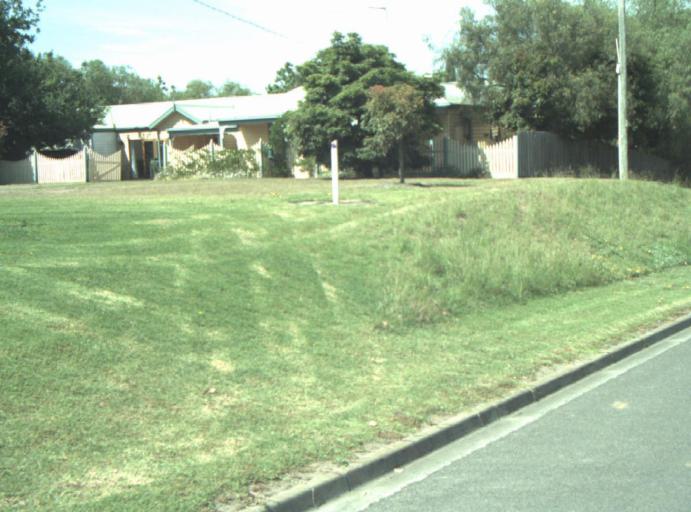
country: AU
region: Victoria
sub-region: Greater Geelong
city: Clifton Springs
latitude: -38.1774
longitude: 144.5653
